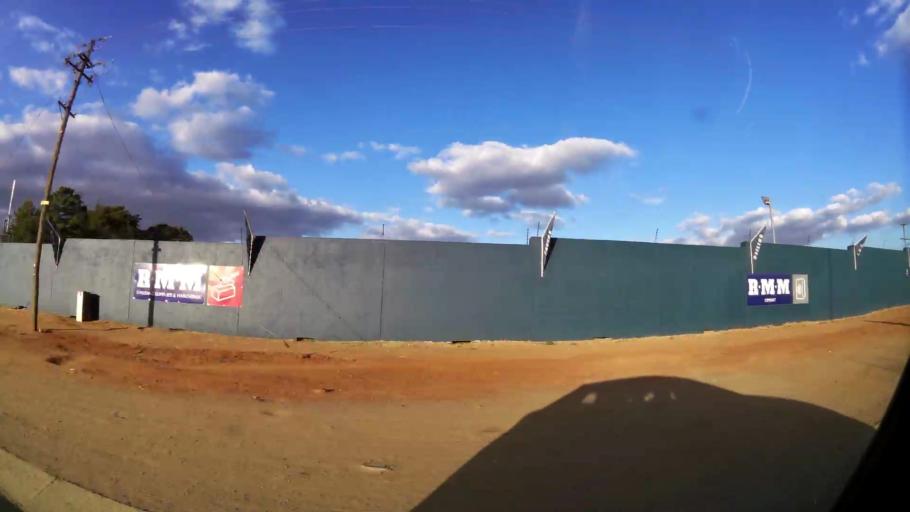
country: ZA
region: Gauteng
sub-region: City of Johannesburg Metropolitan Municipality
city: Midrand
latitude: -25.9570
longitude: 28.1540
